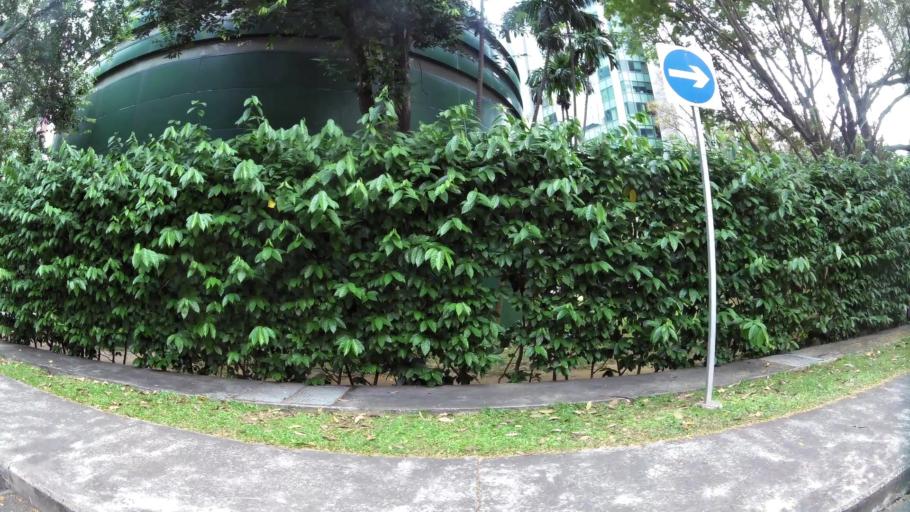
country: SG
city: Singapore
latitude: 1.2744
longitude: 103.8416
